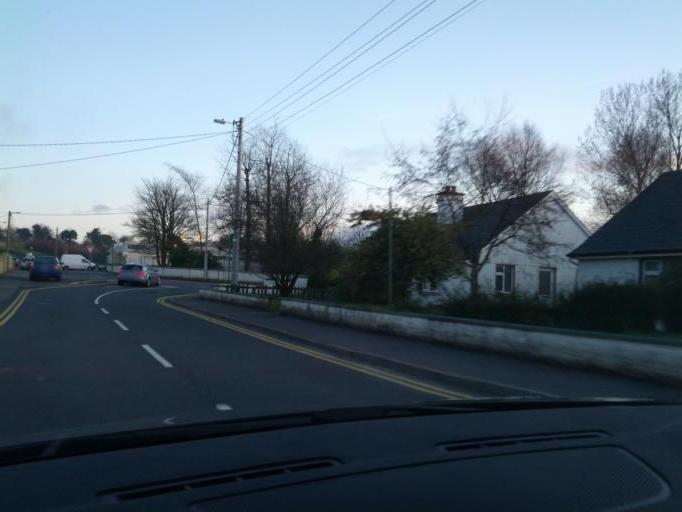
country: IE
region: Connaught
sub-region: Roscommon
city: Boyle
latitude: 53.9705
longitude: -8.2985
